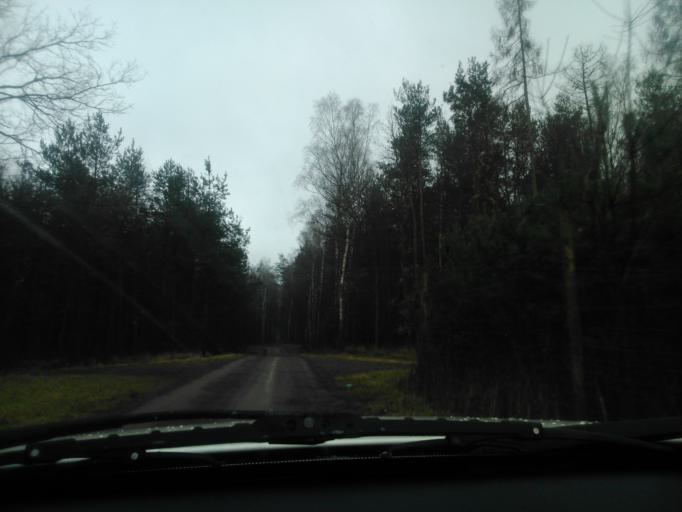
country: PL
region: Kujawsko-Pomorskie
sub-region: Powiat golubsko-dobrzynski
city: Radomin
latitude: 53.1646
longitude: 19.1388
